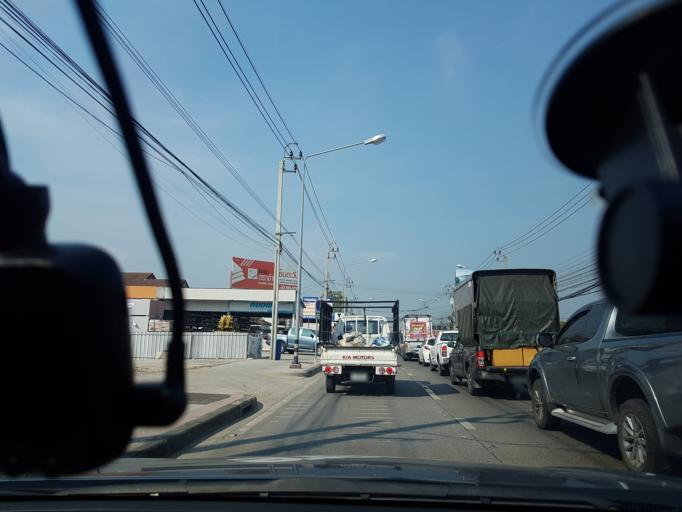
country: TH
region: Bangkok
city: Khlong Sam Wa
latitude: 13.8864
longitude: 100.7222
